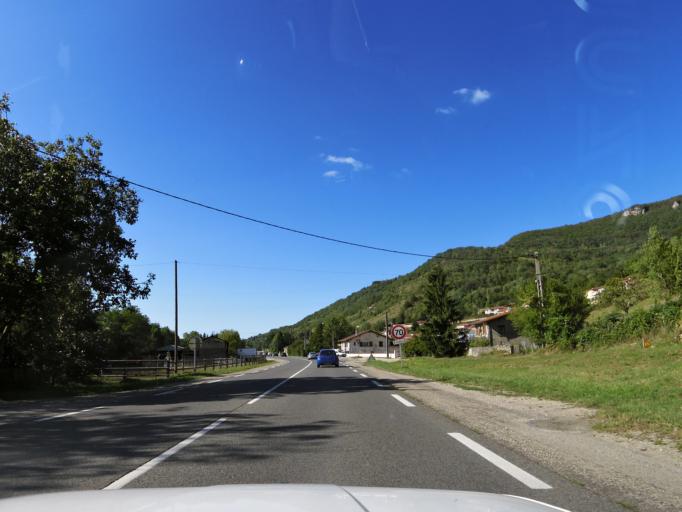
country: FR
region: Rhone-Alpes
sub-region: Departement de l'Ain
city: Vaux-en-Bugey
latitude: 45.9358
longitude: 5.3801
